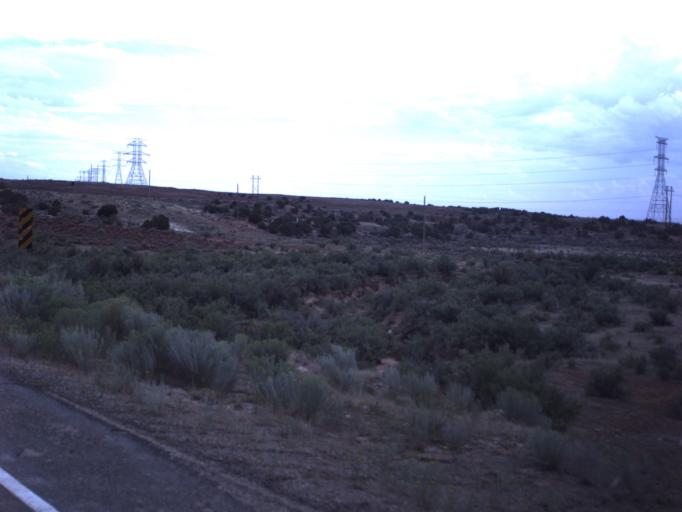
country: US
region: Utah
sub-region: Uintah County
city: Naples
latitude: 40.1657
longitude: -109.3146
